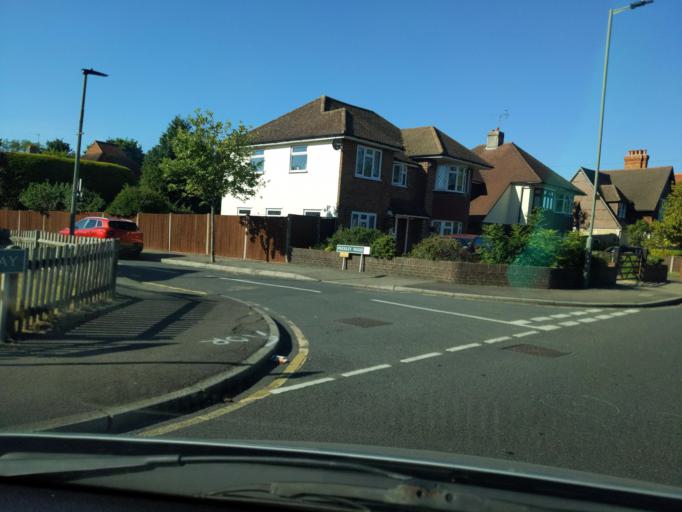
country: GB
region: England
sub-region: Greater London
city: West Wickham
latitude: 51.3756
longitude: 0.0058
